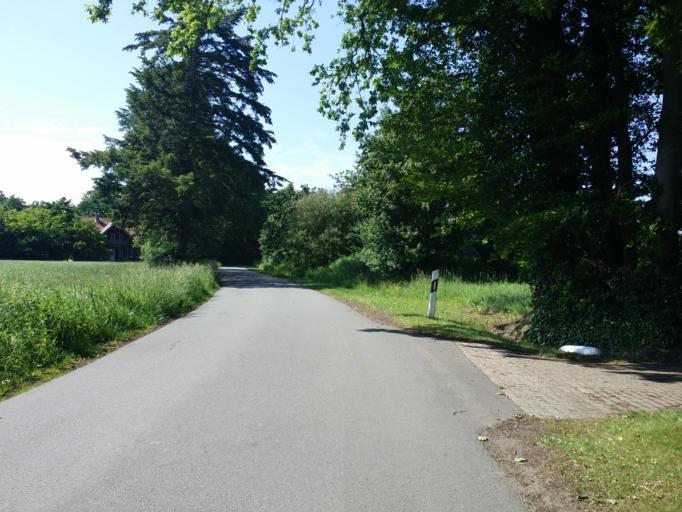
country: DE
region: Lower Saxony
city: Rastede
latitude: 53.2148
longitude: 8.2535
